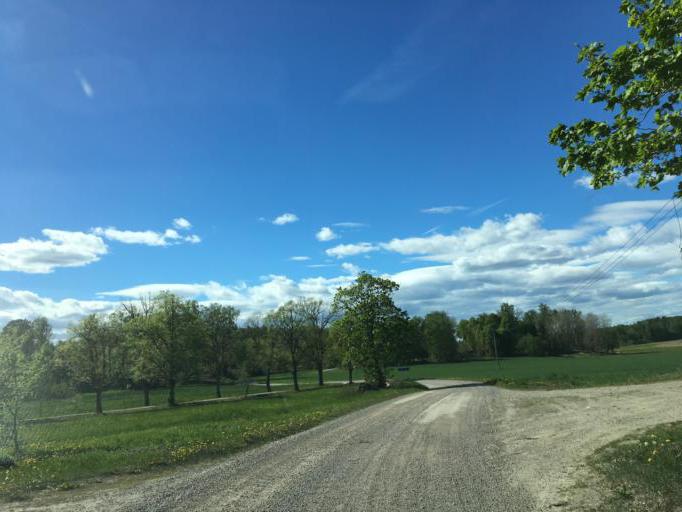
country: SE
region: Soedermanland
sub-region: Eskilstuna Kommun
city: Kvicksund
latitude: 59.3818
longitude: 16.2475
